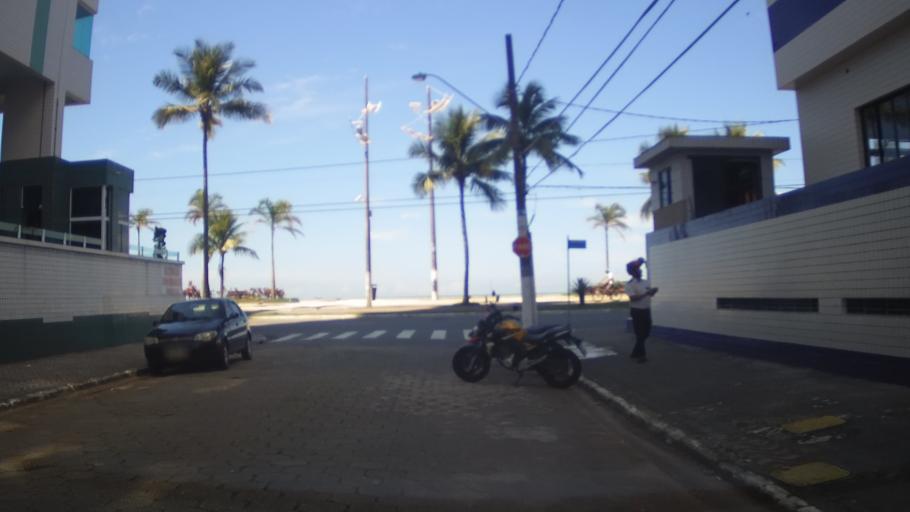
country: BR
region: Sao Paulo
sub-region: Praia Grande
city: Praia Grande
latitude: -24.0155
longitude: -46.4319
